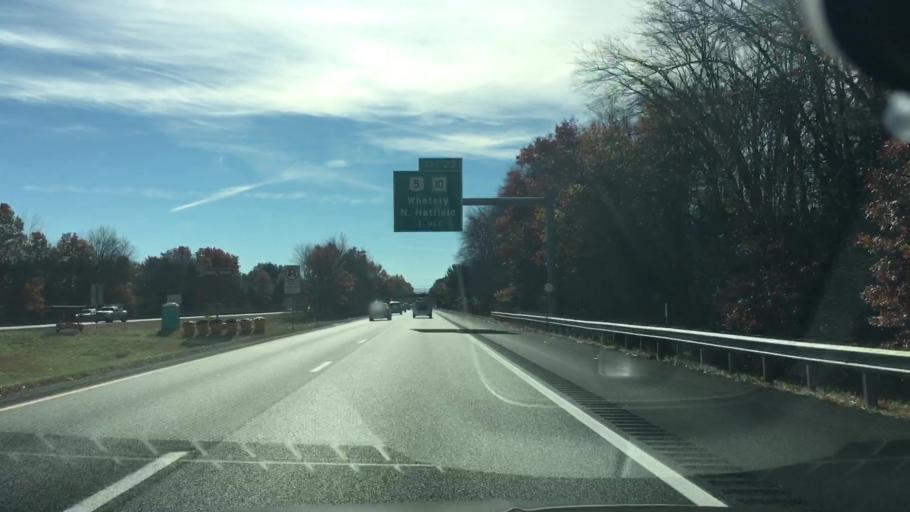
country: US
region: Massachusetts
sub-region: Franklin County
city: Whately
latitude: 42.4491
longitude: -72.6193
